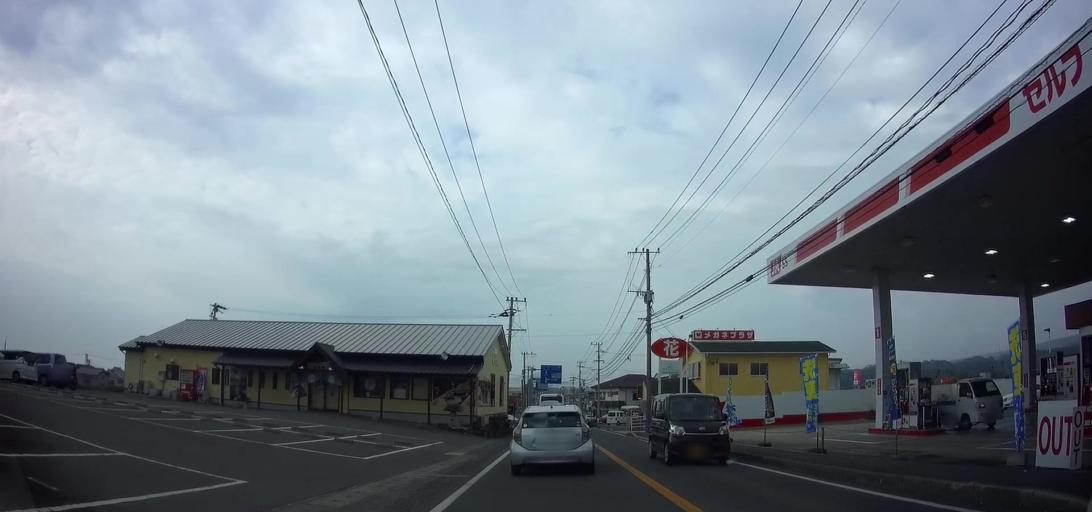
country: JP
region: Nagasaki
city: Shimabara
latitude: 32.6620
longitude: 130.3071
